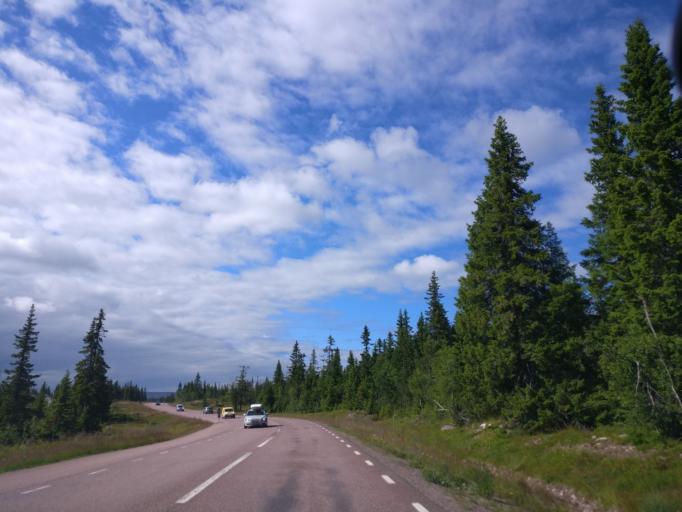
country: SE
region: Dalarna
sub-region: Malung-Saelens kommun
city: Malung
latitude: 61.1618
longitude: 13.1091
